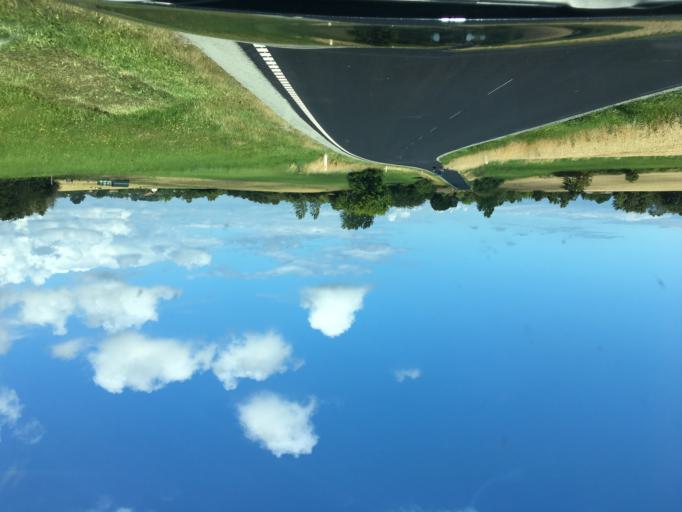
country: DK
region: Capital Region
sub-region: Gribskov Kommune
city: Helsinge
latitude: 56.0652
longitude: 12.2025
